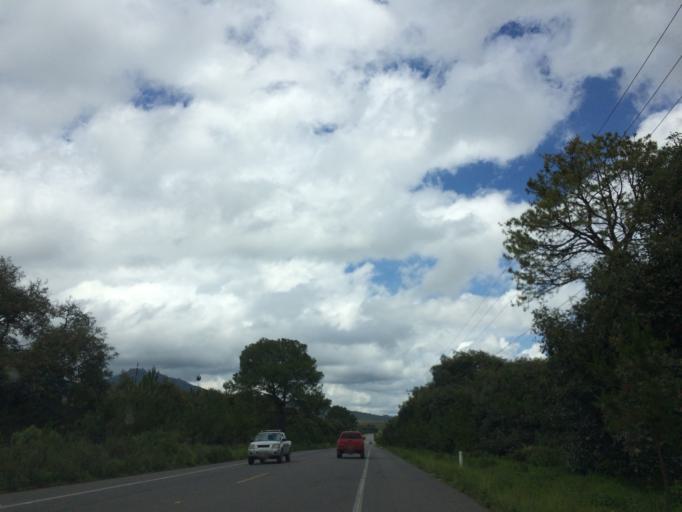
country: MX
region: Michoacan
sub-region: Uruapan
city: Santa Ana Zirosto
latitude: 19.5460
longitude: -102.3180
